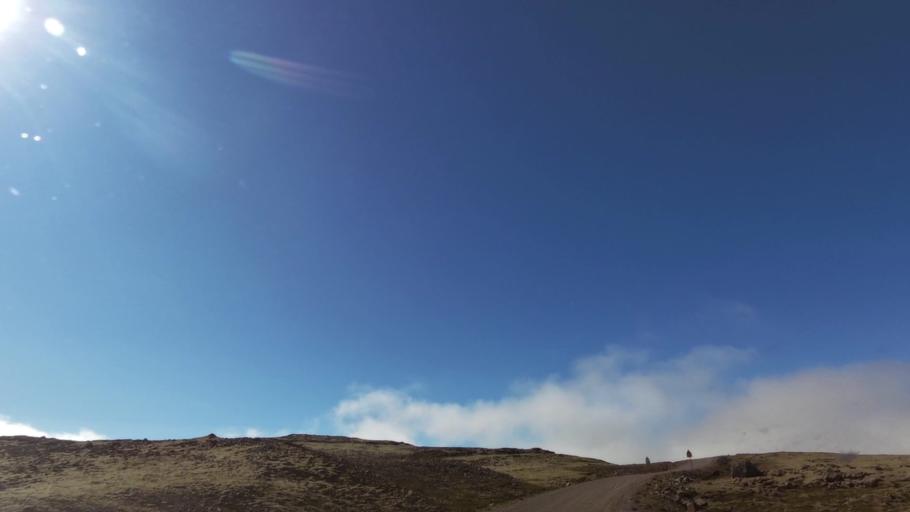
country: IS
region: West
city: Olafsvik
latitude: 65.5513
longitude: -24.2167
